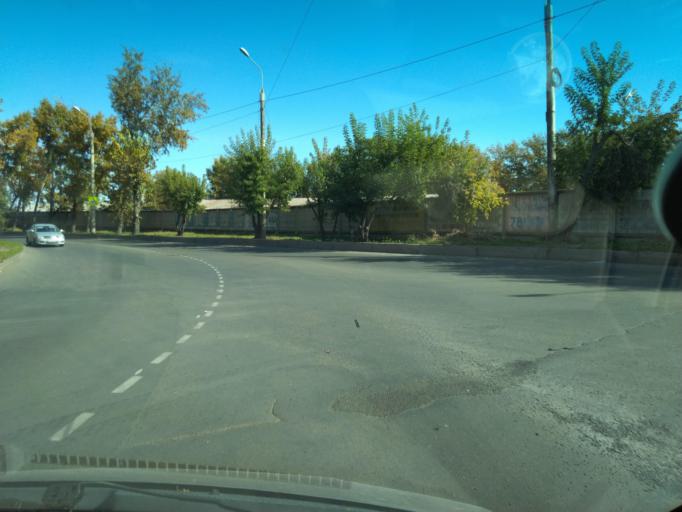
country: RU
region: Krasnoyarskiy
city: Krasnoyarsk
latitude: 56.0066
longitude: 92.9693
